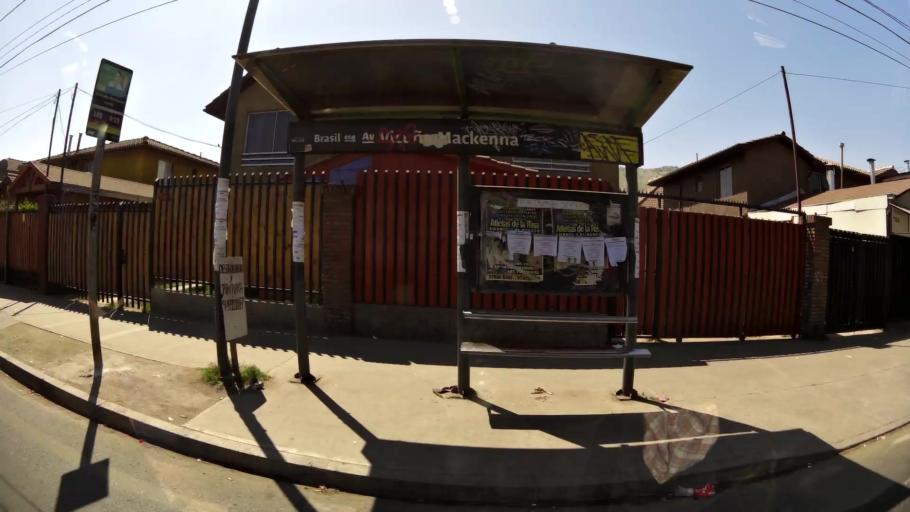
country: CL
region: Santiago Metropolitan
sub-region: Provincia de Santiago
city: Lo Prado
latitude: -33.3998
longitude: -70.7462
